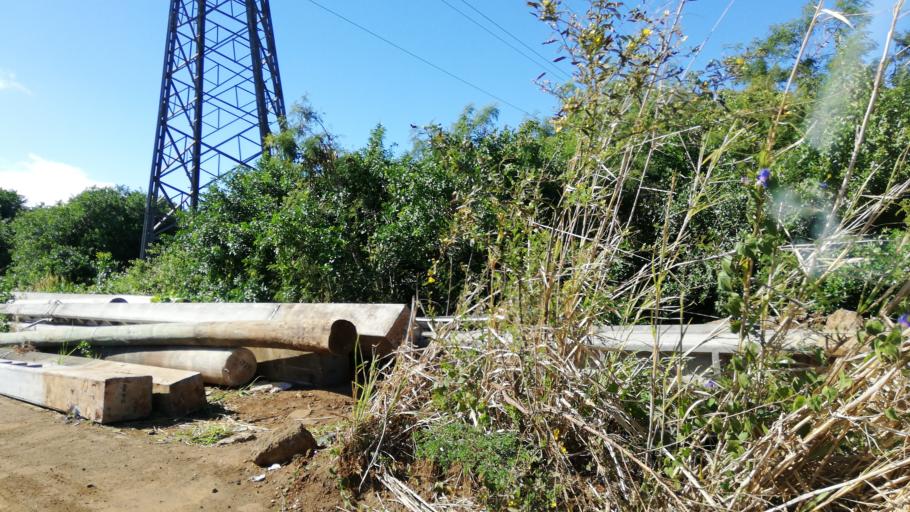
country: MU
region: Plaines Wilhems
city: Ebene
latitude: -20.2408
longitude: 57.4796
